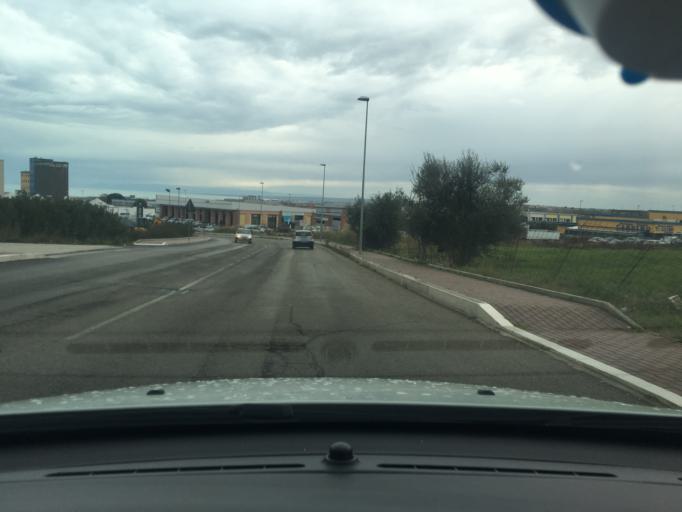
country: IT
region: Molise
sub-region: Provincia di Campobasso
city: Termoli
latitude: 41.9821
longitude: 15.0019
